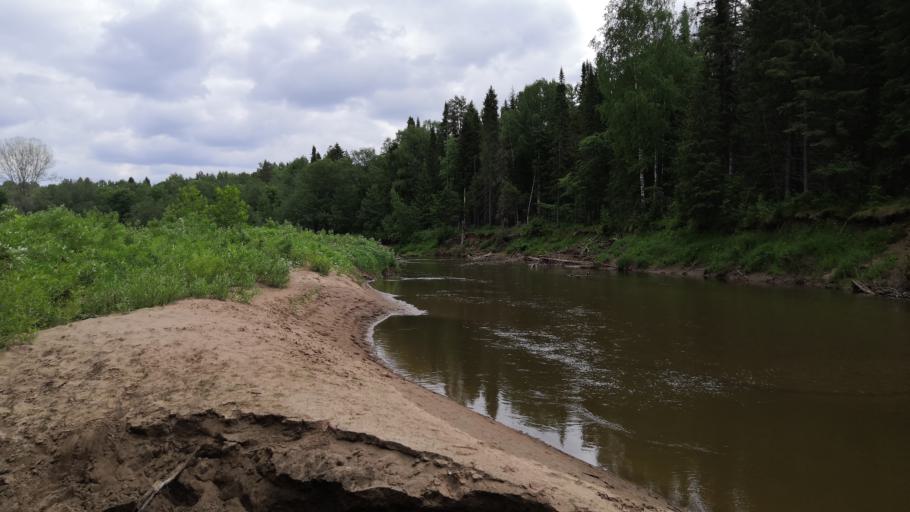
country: RU
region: Udmurtiya
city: Kez
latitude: 57.8354
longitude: 53.6799
